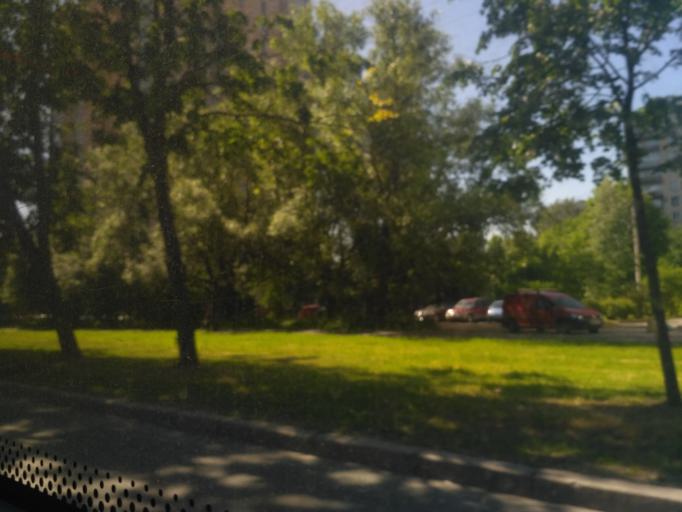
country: RU
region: Leningrad
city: Kalininskiy
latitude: 59.9677
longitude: 30.4127
